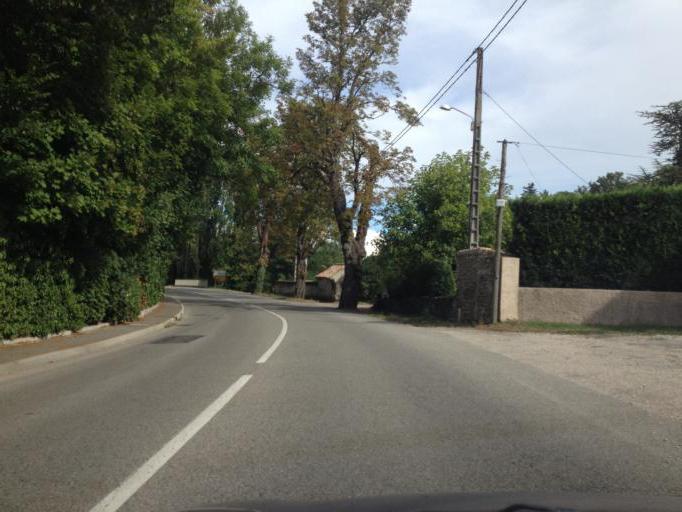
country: FR
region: Rhone-Alpes
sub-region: Departement de la Drome
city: Grignan
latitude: 44.4164
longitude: 4.9115
